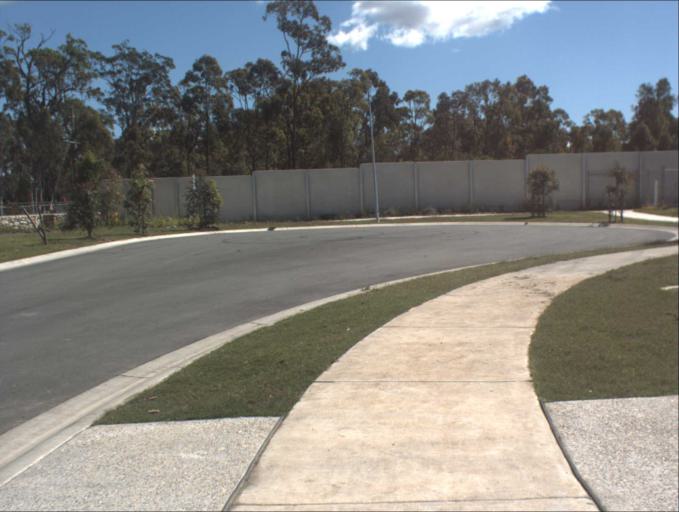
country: AU
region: Queensland
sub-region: Logan
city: Chambers Flat
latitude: -27.7964
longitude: 153.1006
